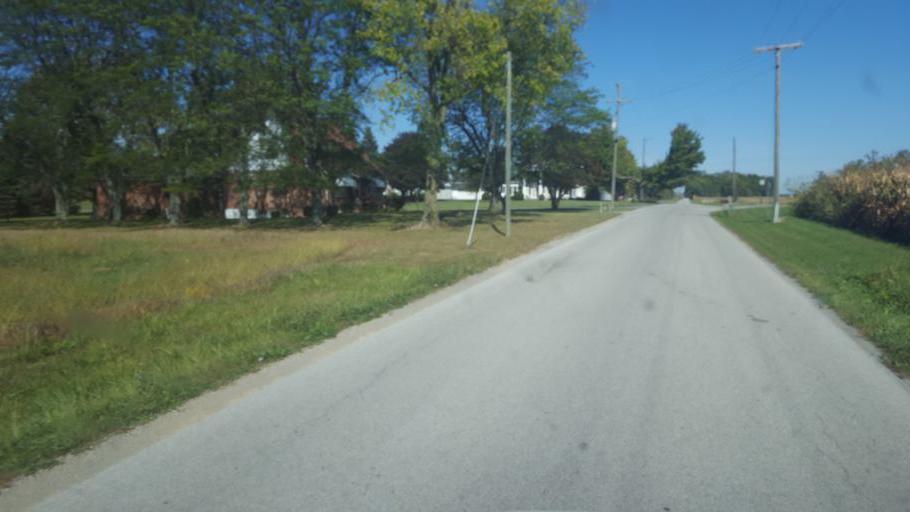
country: US
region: Ohio
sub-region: Wyandot County
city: Upper Sandusky
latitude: 40.8468
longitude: -83.2369
